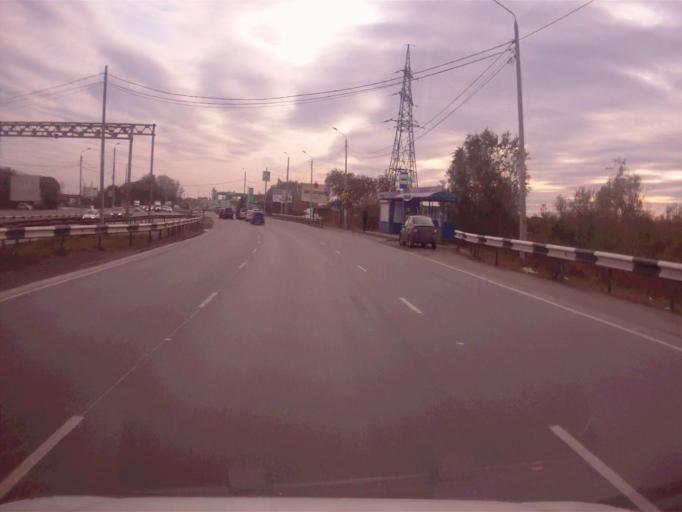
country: RU
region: Chelyabinsk
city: Novosineglazovskiy
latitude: 55.0738
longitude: 61.3881
